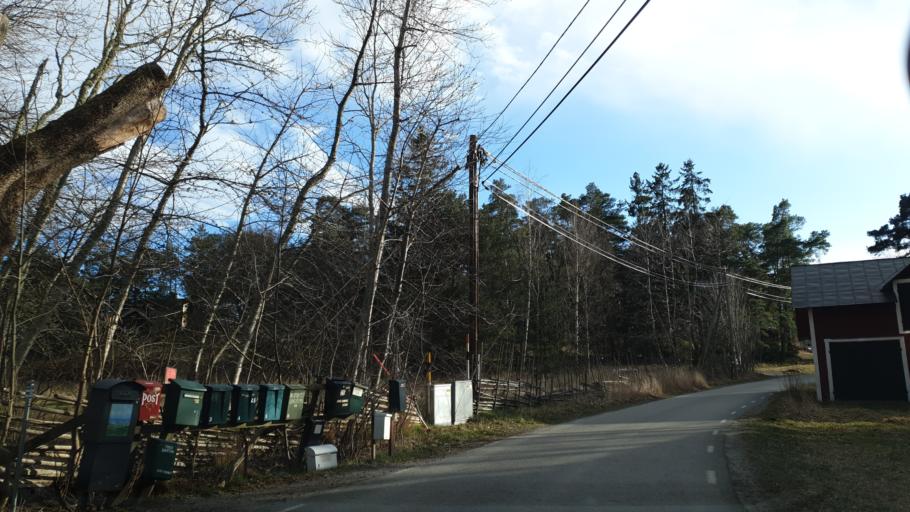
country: SE
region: Stockholm
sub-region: Varmdo Kommun
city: Holo
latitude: 59.3074
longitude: 18.6917
